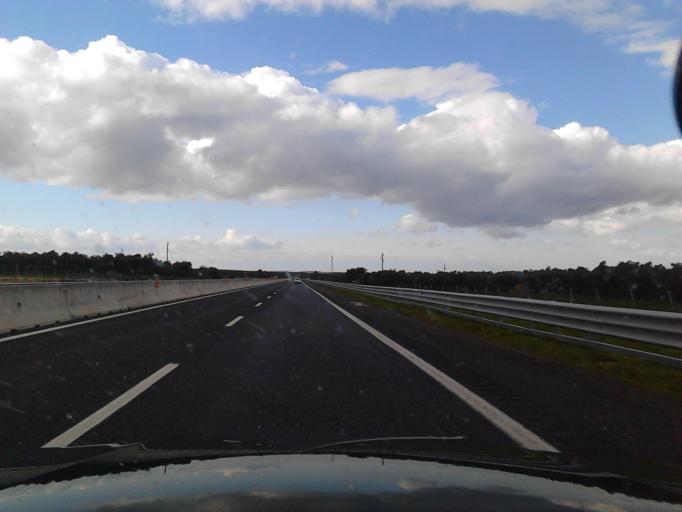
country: IT
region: Apulia
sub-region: Provincia di Barletta - Andria - Trani
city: Andria
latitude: 41.2571
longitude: 16.2785
